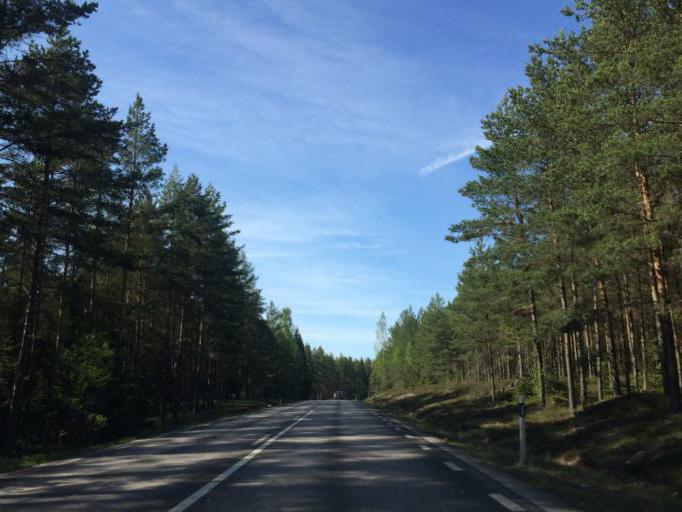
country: SE
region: Soedermanland
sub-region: Katrineholms Kommun
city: Katrineholm
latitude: 59.1041
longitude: 16.1806
